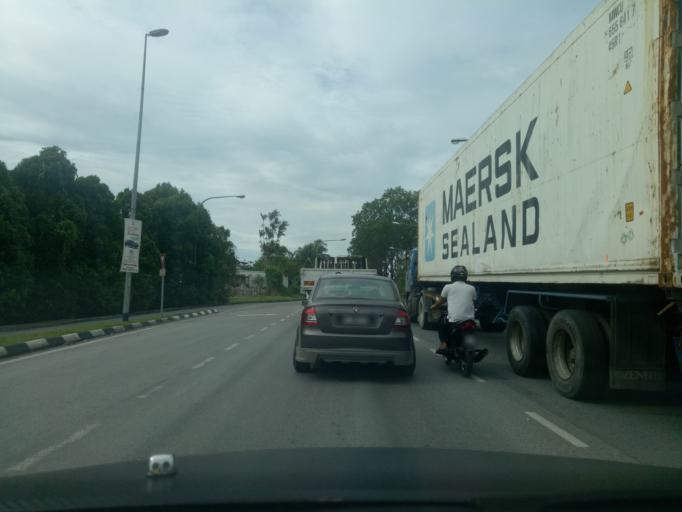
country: MY
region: Sarawak
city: Kuching
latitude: 1.5419
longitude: 110.3713
